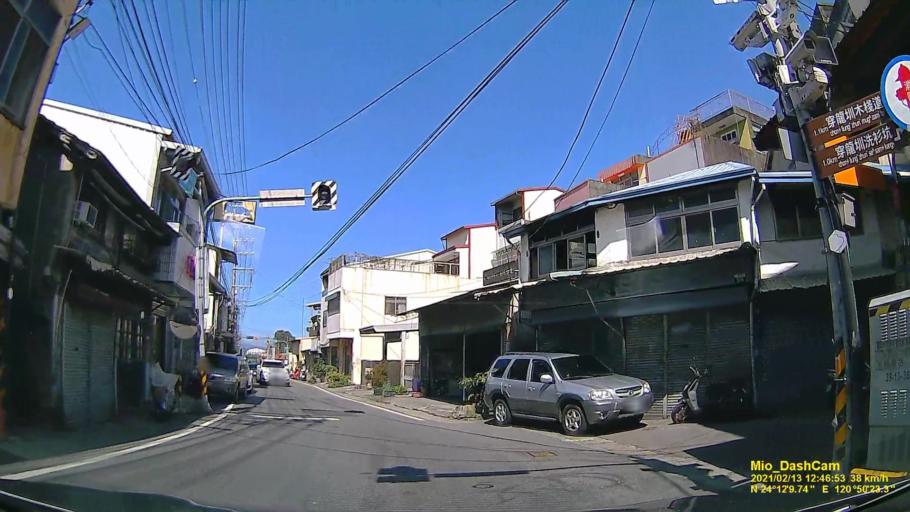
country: TW
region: Taiwan
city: Fengyuan
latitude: 24.2027
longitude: 120.8398
